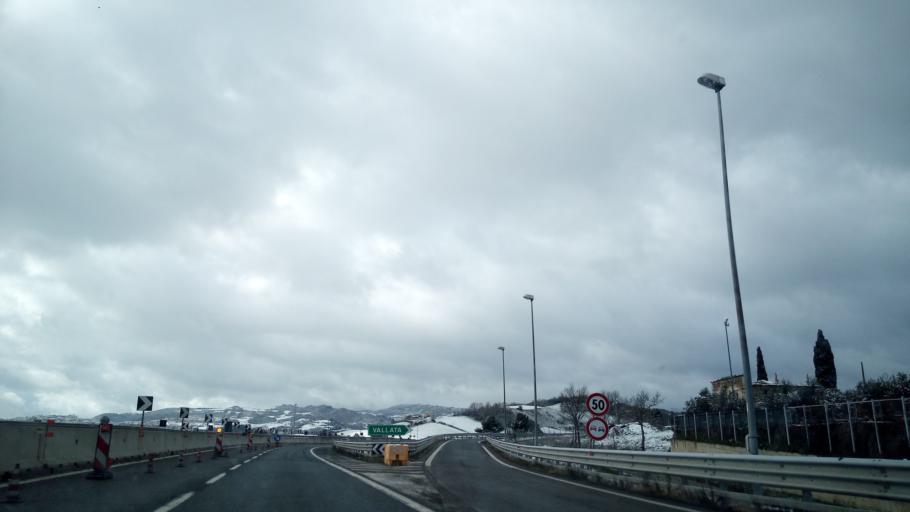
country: IT
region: Campania
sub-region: Provincia di Avellino
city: Scampitella
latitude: 41.0601
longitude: 15.2930
